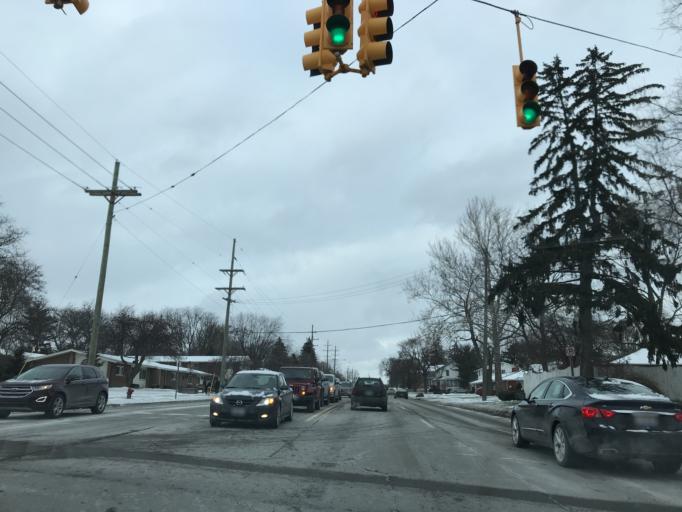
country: US
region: Michigan
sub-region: Wayne County
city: Plymouth
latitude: 42.3747
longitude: -83.4804
